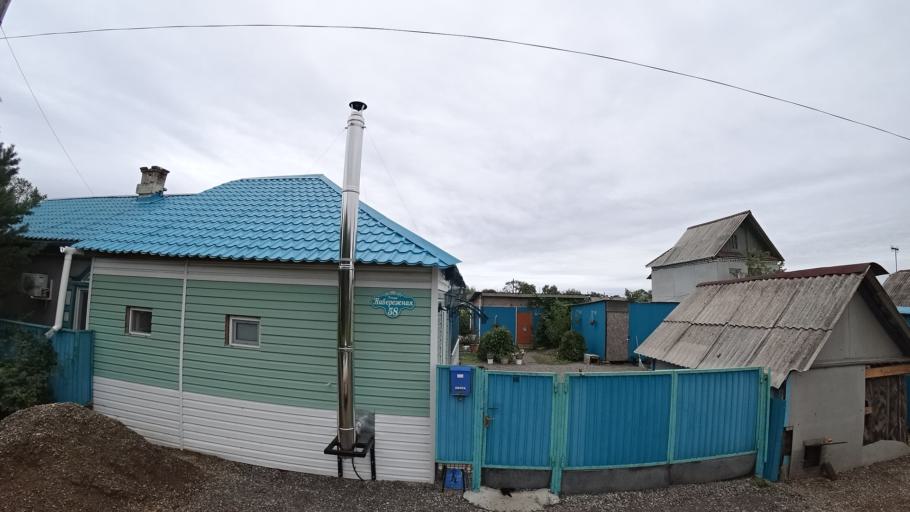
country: RU
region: Primorskiy
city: Chernigovka
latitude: 44.3485
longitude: 132.5790
